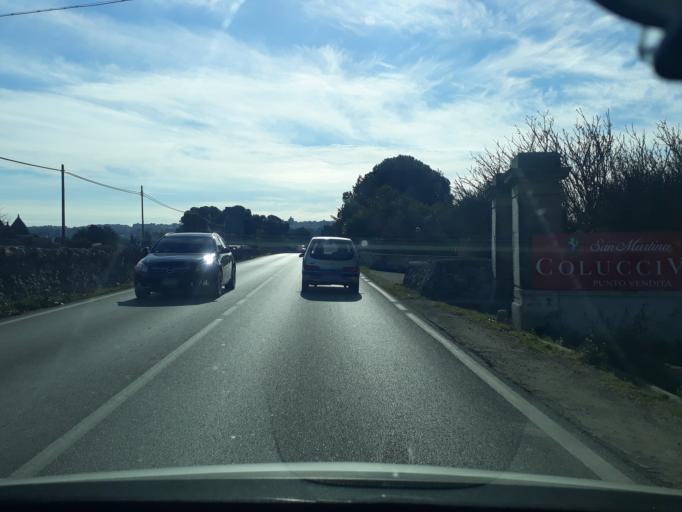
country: IT
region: Apulia
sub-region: Provincia di Taranto
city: Martina Franca
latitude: 40.7265
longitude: 17.3326
